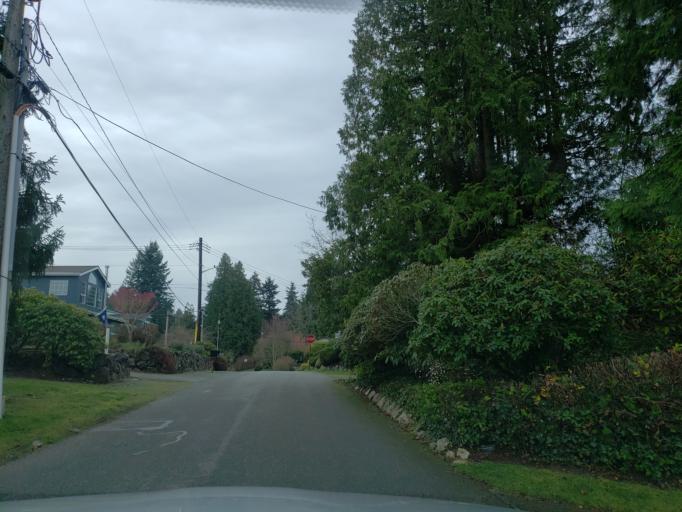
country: US
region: Washington
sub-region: Snohomish County
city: Edmonds
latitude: 47.8274
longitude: -122.3590
